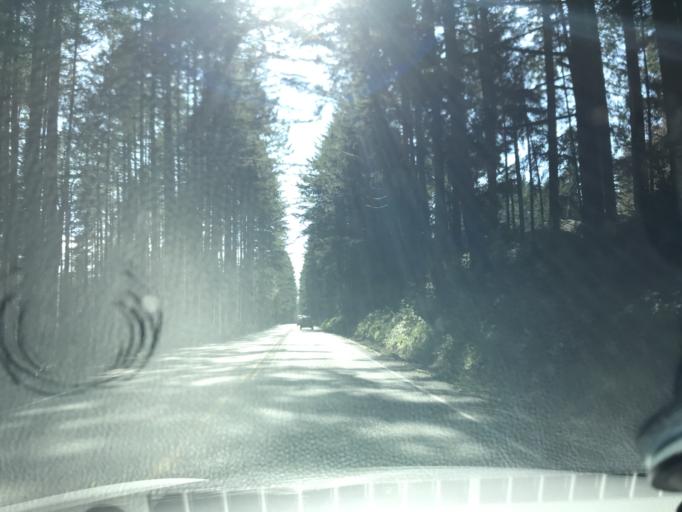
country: US
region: Washington
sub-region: Pierce County
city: Key Center
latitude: 47.3561
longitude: -122.7326
